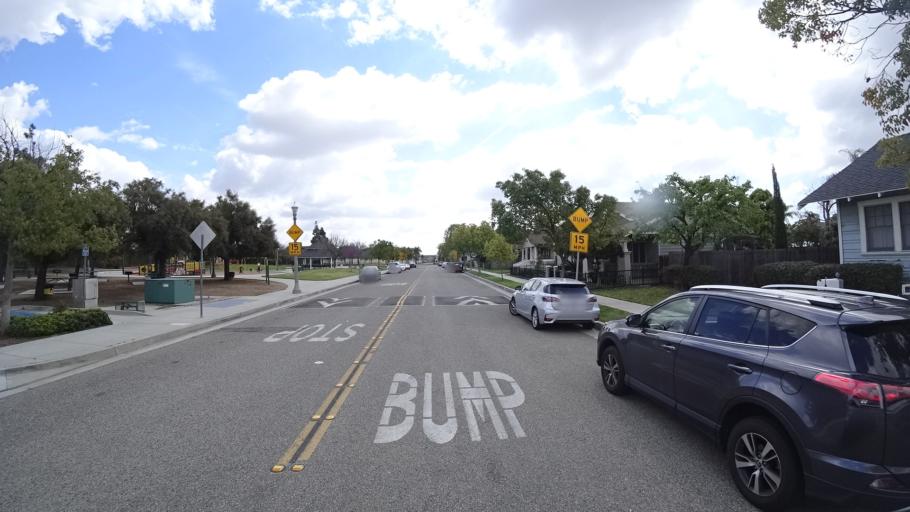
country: US
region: California
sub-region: Orange County
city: Anaheim
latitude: 33.8364
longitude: -117.9069
